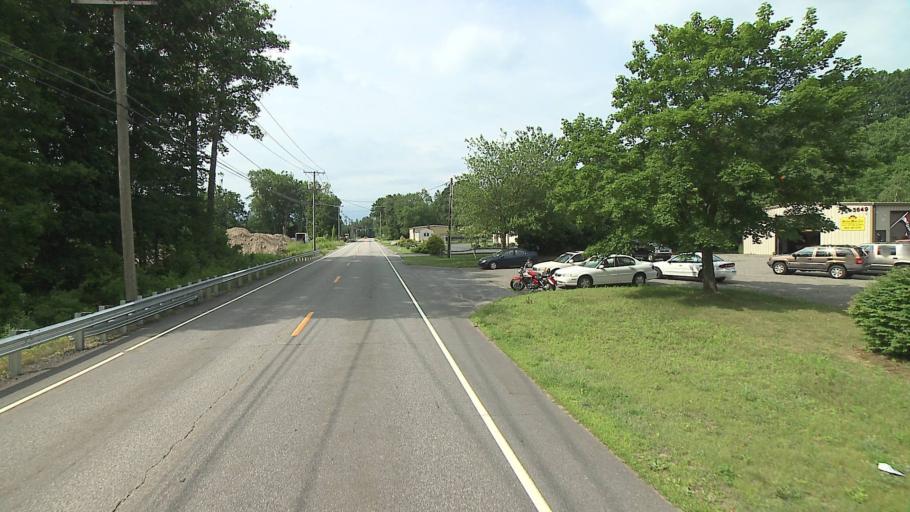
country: US
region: Connecticut
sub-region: Litchfield County
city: Winsted
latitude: 41.8832
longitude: -73.0754
